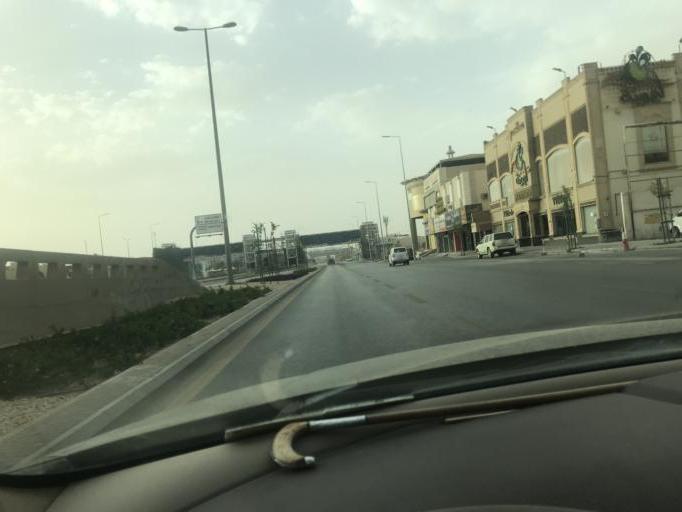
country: SA
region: Ar Riyad
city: Riyadh
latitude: 24.7776
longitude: 46.6648
